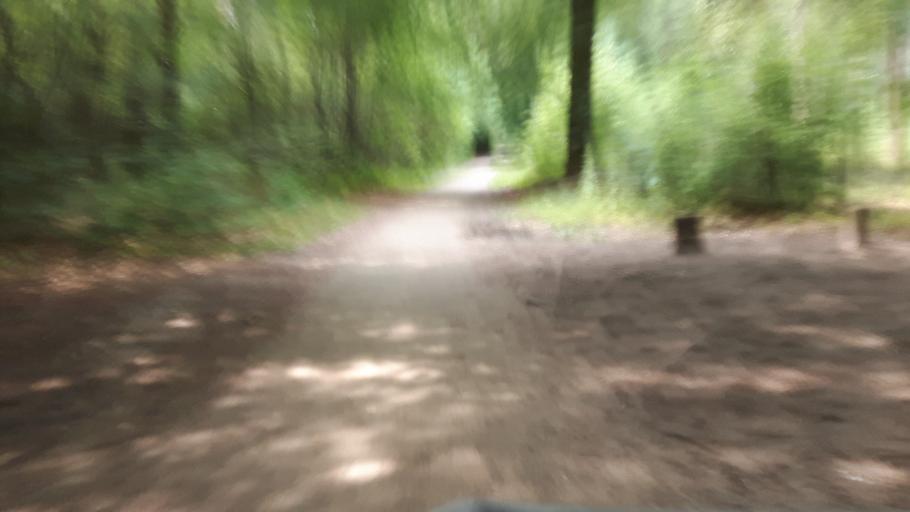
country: NL
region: North Holland
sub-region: Gemeente Hilversum
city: Hilversum
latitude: 52.1828
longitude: 5.1901
